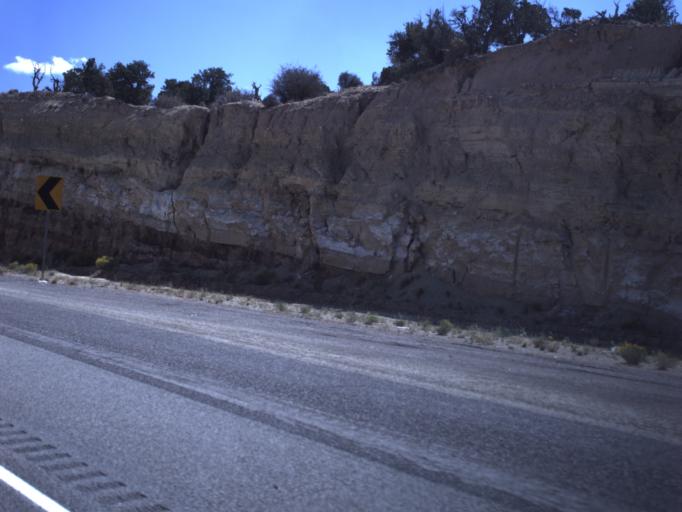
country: US
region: Utah
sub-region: Emery County
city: Ferron
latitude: 38.8499
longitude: -110.9049
